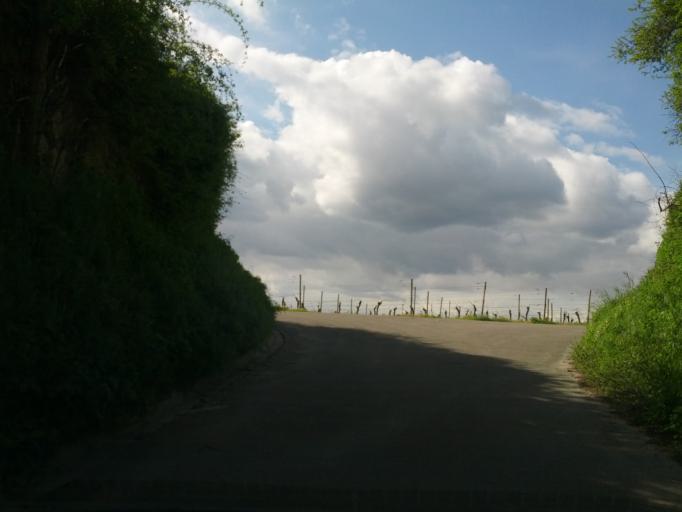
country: DE
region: Baden-Wuerttemberg
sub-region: Freiburg Region
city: Merdingen
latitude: 47.9750
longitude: 7.6806
